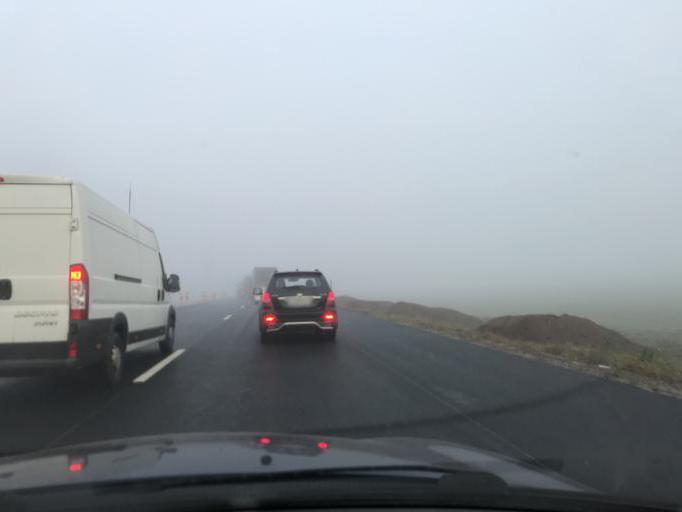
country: BY
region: Minsk
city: Valozhyn
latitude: 54.0636
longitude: 26.5271
